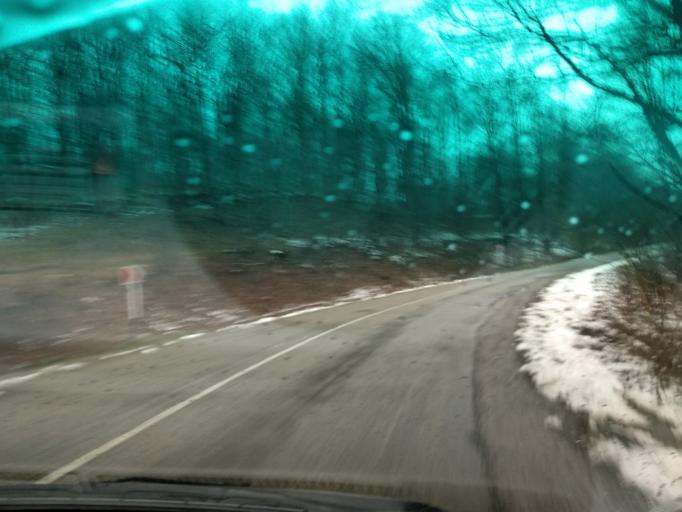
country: RU
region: Krasnodarskiy
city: Khadyzhensk
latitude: 44.2283
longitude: 39.3835
